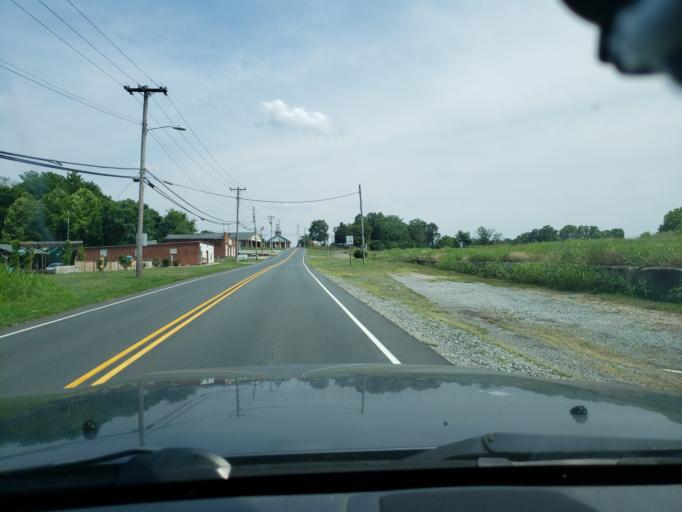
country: US
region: North Carolina
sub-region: Alamance County
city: Swepsonville
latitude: 36.0241
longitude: -79.3639
